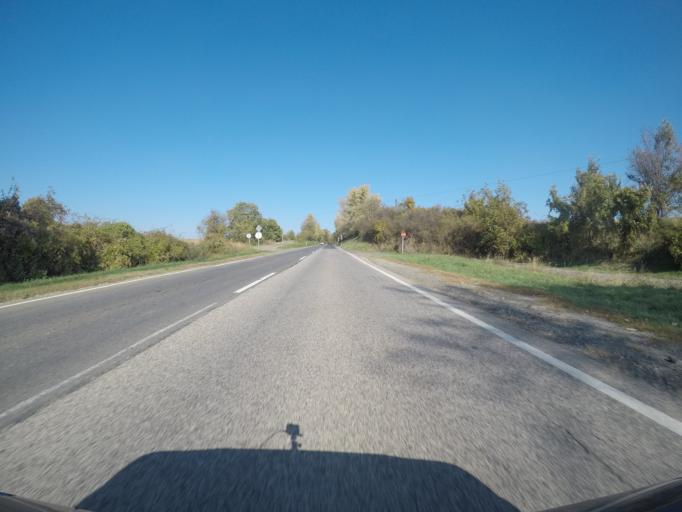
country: HU
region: Baranya
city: Pecsvarad
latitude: 46.1836
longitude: 18.4473
